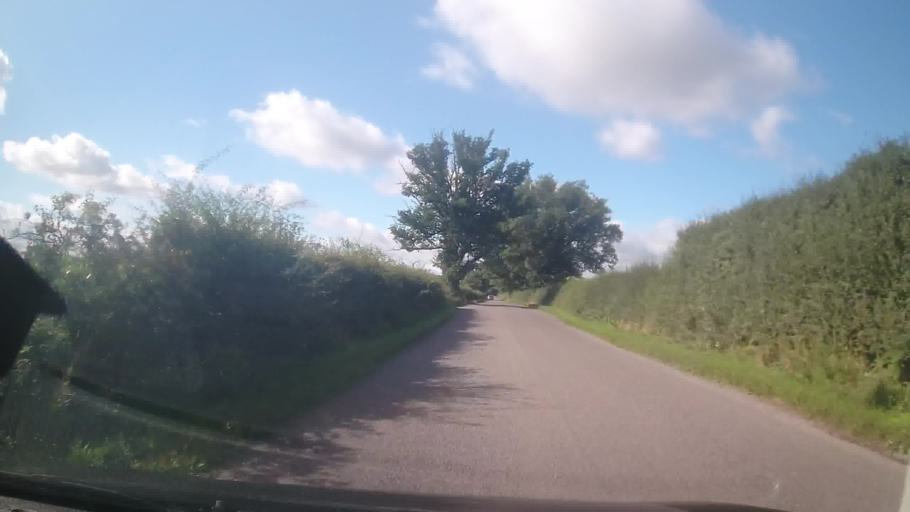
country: GB
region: England
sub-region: Shropshire
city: Bicton
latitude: 52.7440
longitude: -2.8414
